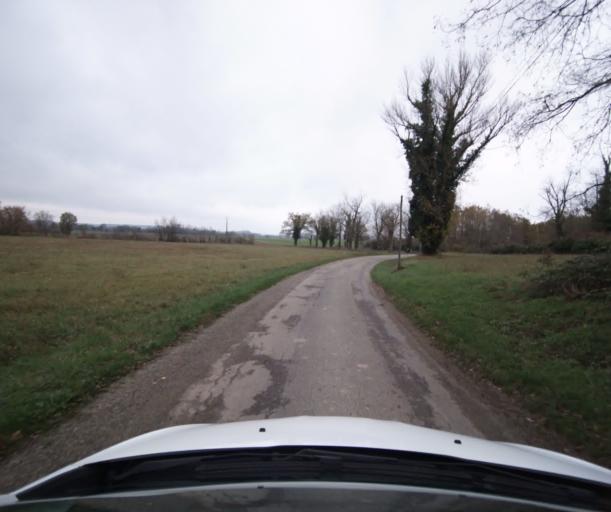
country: FR
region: Midi-Pyrenees
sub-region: Departement du Tarn-et-Garonne
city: Moissac
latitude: 44.0772
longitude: 1.1369
